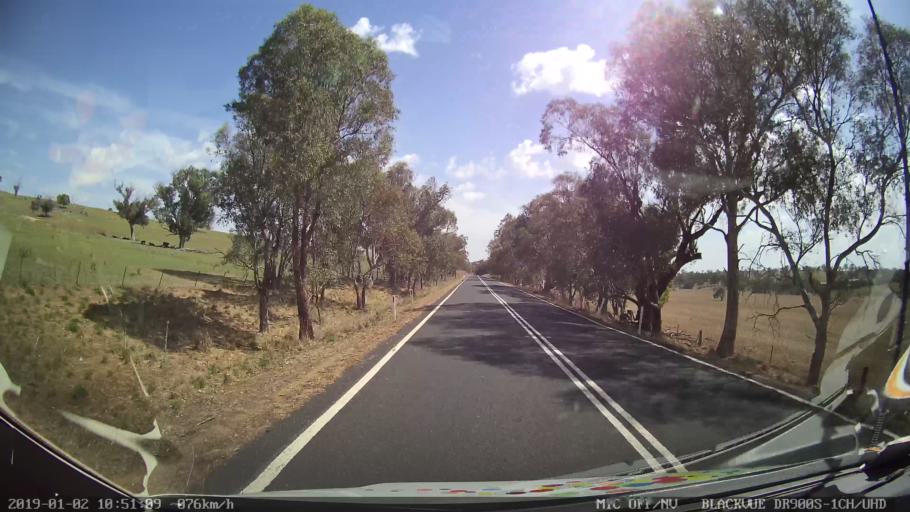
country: AU
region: New South Wales
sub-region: Cootamundra
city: Cootamundra
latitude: -34.7035
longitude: 148.2763
